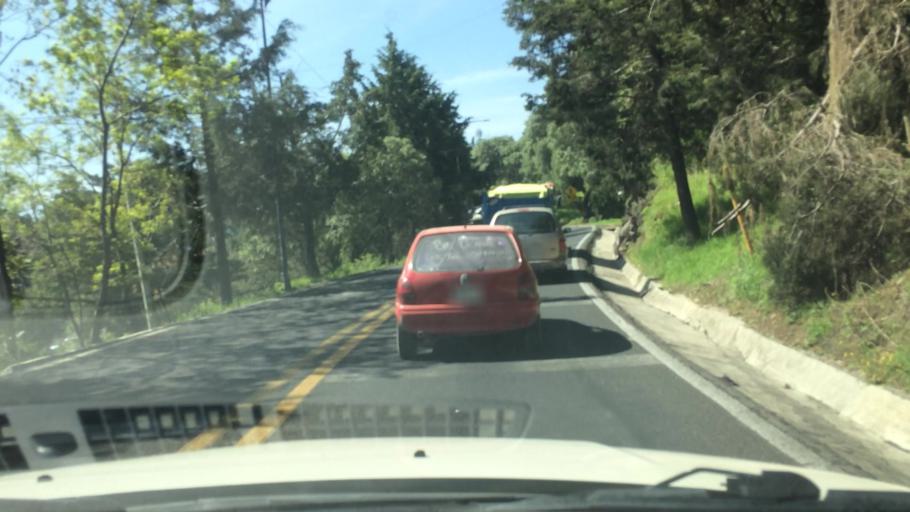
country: MX
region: Mexico City
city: Xochimilco
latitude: 19.2374
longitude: -99.1595
